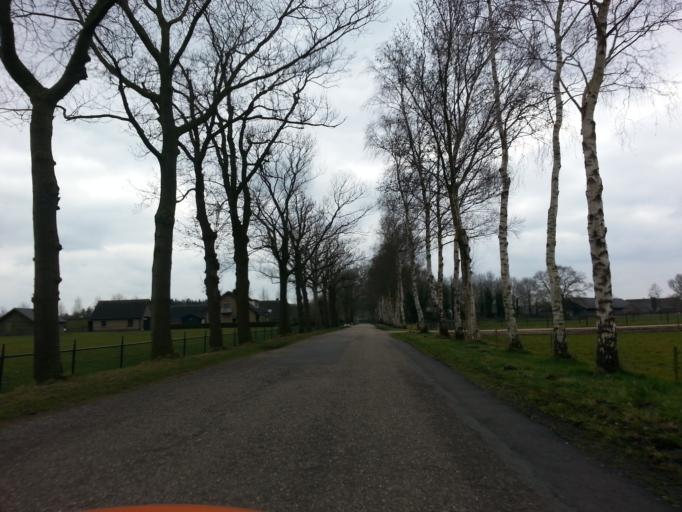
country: NL
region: Gelderland
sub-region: Gemeente Barneveld
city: Terschuur
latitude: 52.1062
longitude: 5.4991
